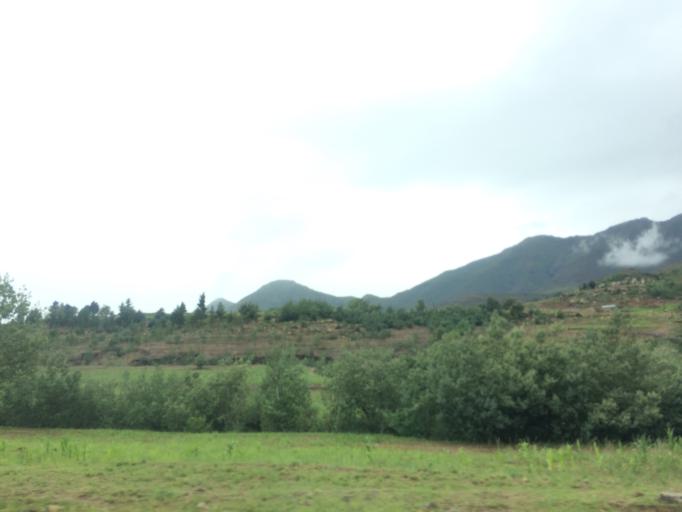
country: LS
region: Mafeteng
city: Mafeteng
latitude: -29.7835
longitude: 27.5222
